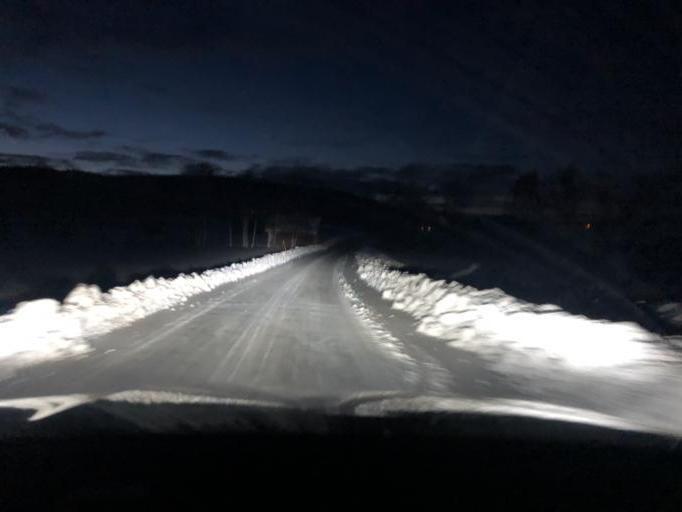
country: SE
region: Vaesternorrland
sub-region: Kramfors Kommun
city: Bollstabruk
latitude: 63.0537
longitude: 17.6414
